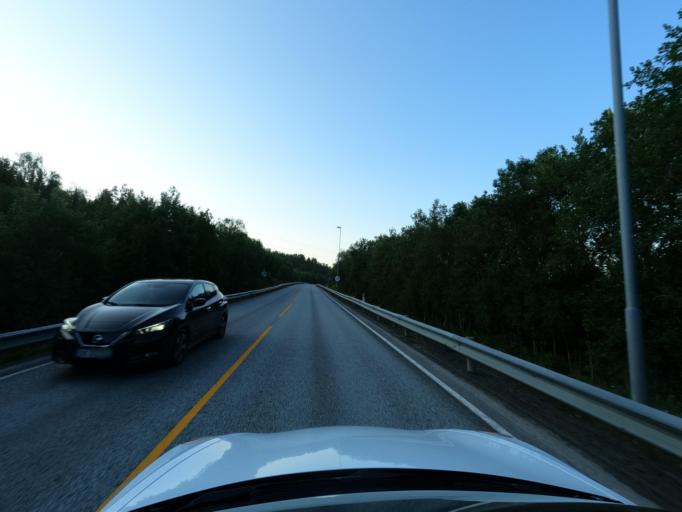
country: NO
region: Troms
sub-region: Harstad
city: Harstad
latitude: 68.7348
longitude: 16.5532
